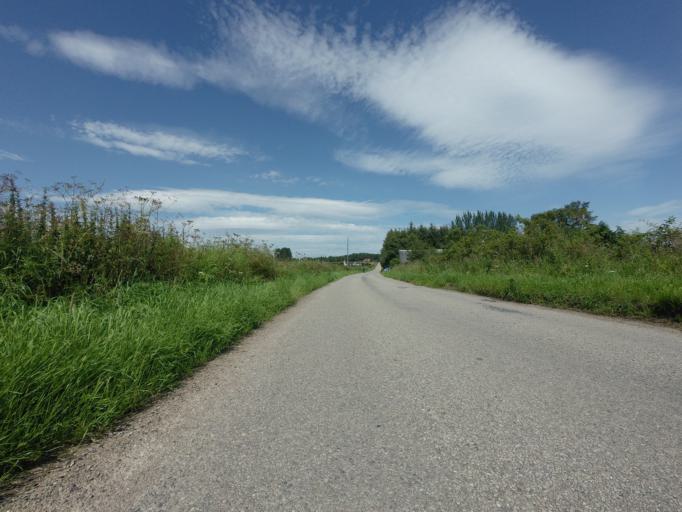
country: GB
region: Scotland
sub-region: Highland
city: Inverness
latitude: 57.5270
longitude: -4.3183
